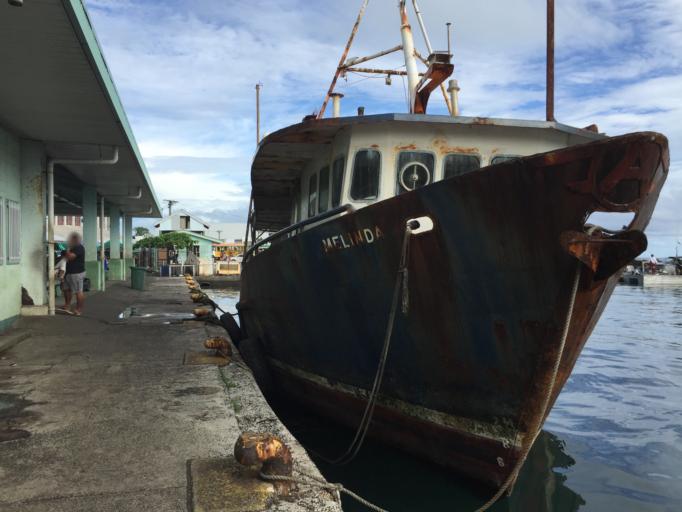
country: WS
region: Tuamasaga
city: Apia
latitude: -13.8294
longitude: -171.7699
